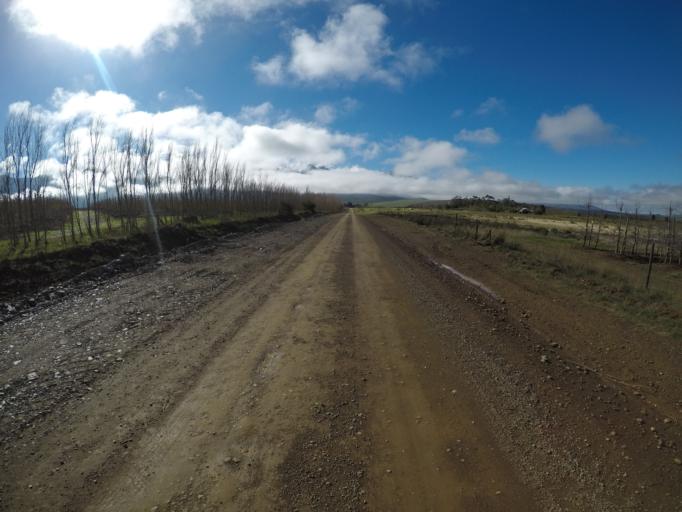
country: ZA
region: Western Cape
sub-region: Overberg District Municipality
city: Caledon
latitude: -34.1160
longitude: 19.7399
